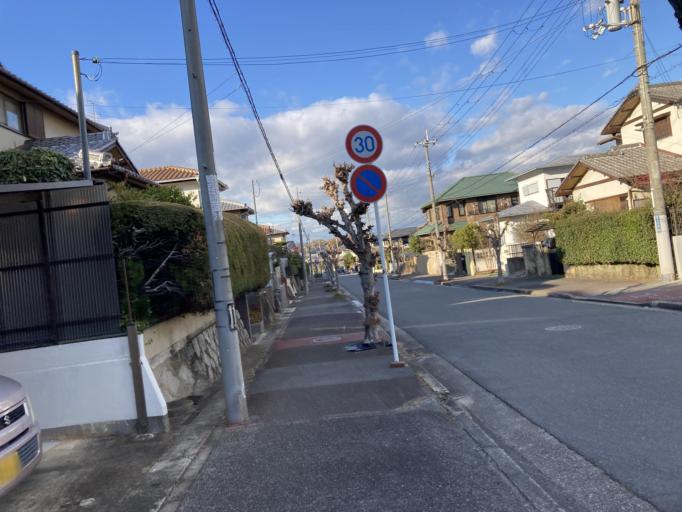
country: JP
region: Nara
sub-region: Ikoma-shi
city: Ikoma
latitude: 34.6823
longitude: 135.7288
